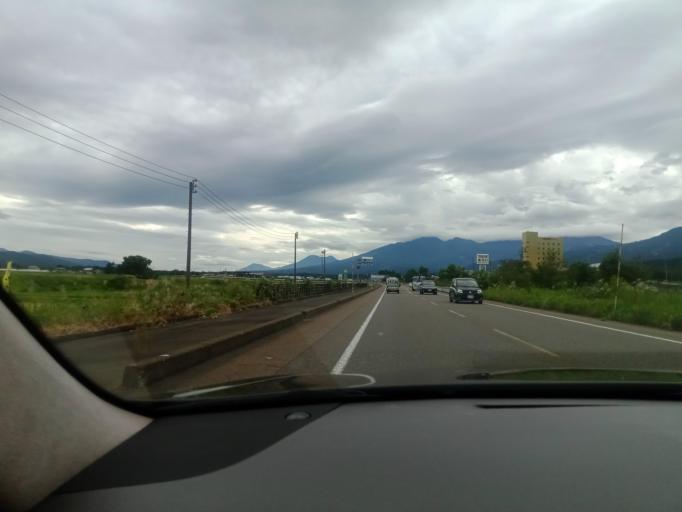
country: JP
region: Niigata
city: Arai
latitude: 37.0308
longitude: 138.2302
